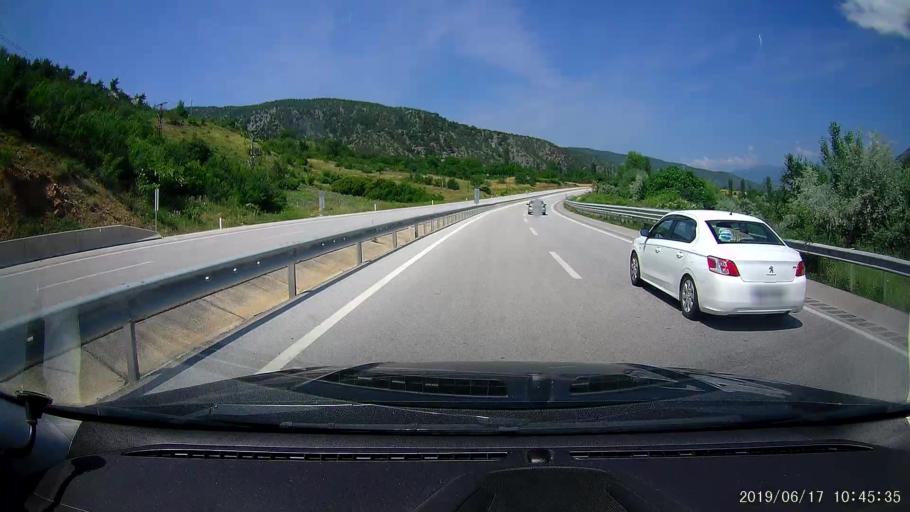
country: TR
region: Corum
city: Hacihamza
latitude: 41.0623
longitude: 34.4840
